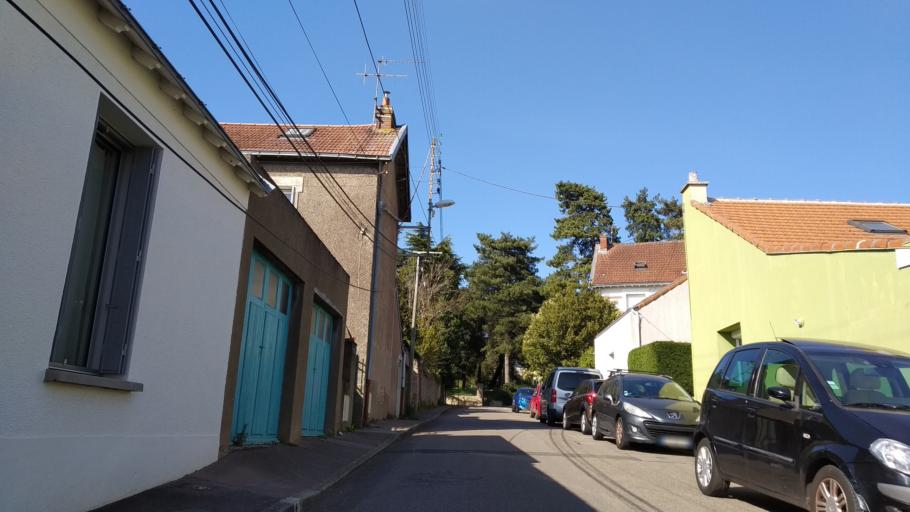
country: FR
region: Pays de la Loire
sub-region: Departement de la Loire-Atlantique
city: Bouguenais
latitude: 47.1999
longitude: -1.5986
